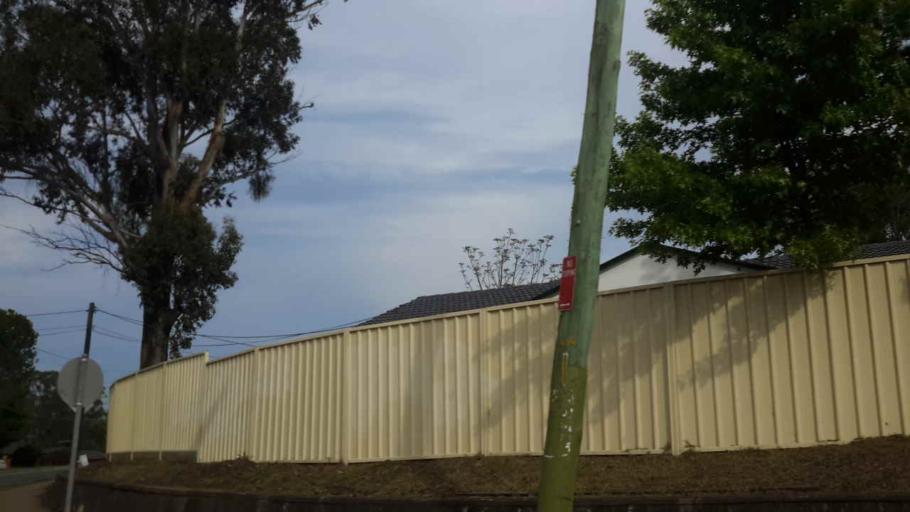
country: AU
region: New South Wales
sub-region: Penrith Municipality
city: Cambridge Park
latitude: -33.7469
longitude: 150.7143
